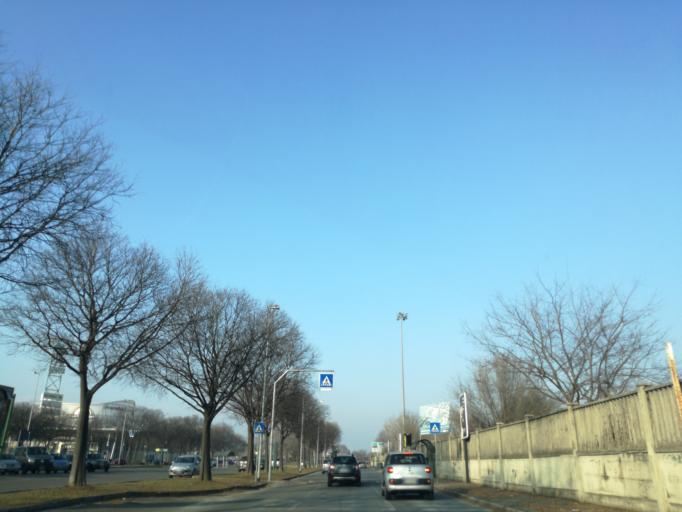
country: IT
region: Piedmont
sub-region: Provincia di Torino
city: Lesna
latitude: 45.0567
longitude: 7.6154
